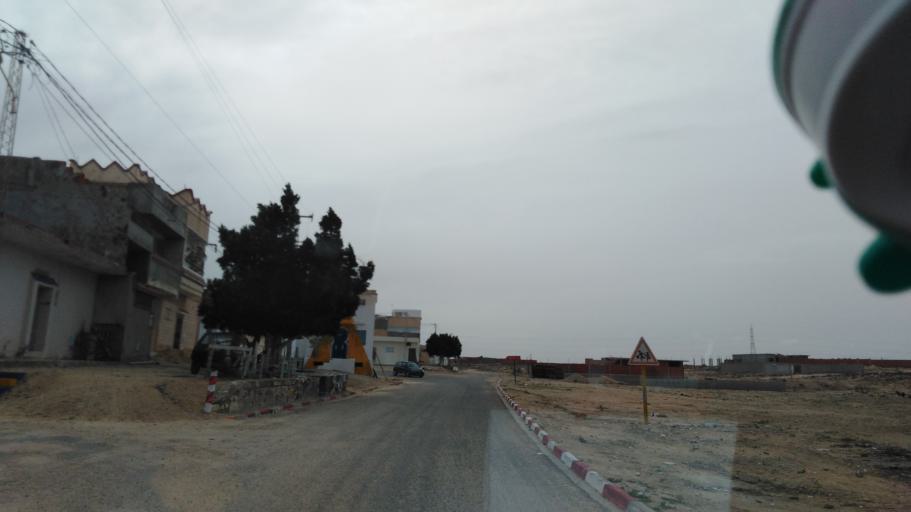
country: TN
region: Qabis
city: Gabes
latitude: 33.9506
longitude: 10.0026
